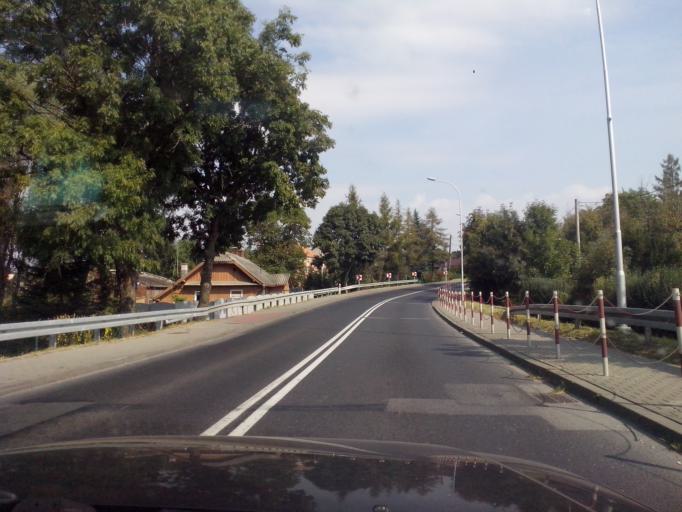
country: PL
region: Subcarpathian Voivodeship
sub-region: Powiat rzeszowski
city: Lutoryz
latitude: 49.9753
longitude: 21.9247
